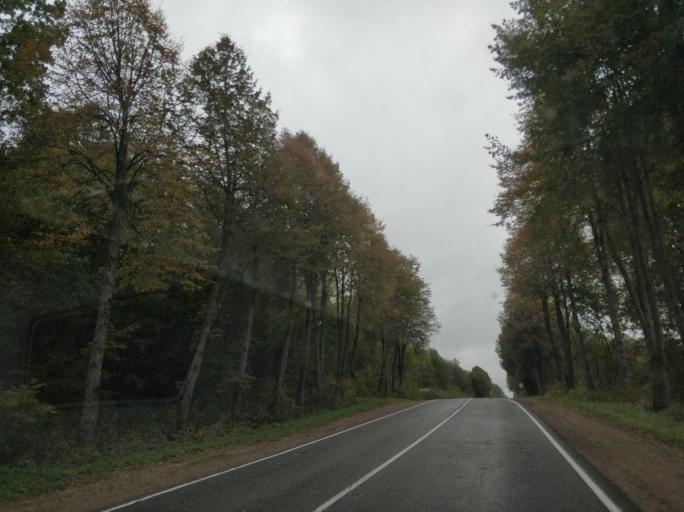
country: RU
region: Pskov
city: Opochka
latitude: 56.5579
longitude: 28.6303
